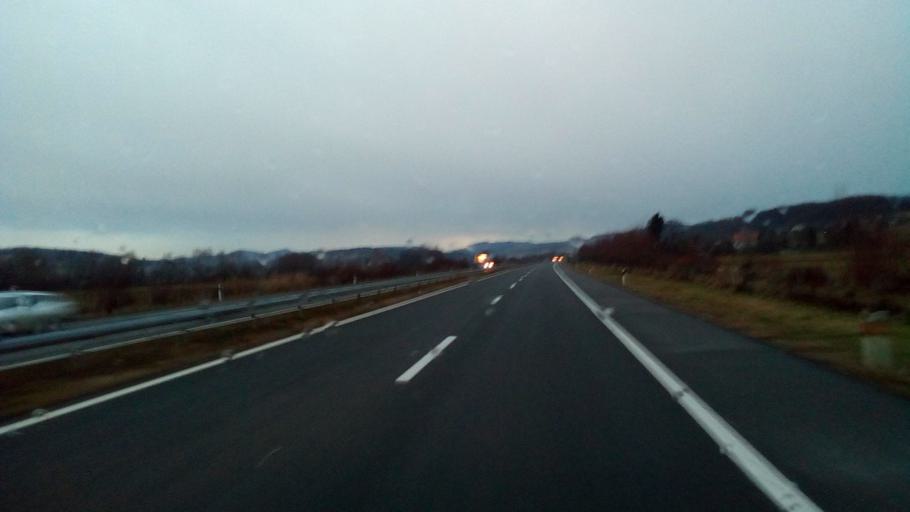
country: HR
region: Varazdinska
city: Remetinec
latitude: 46.0456
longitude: 16.2964
